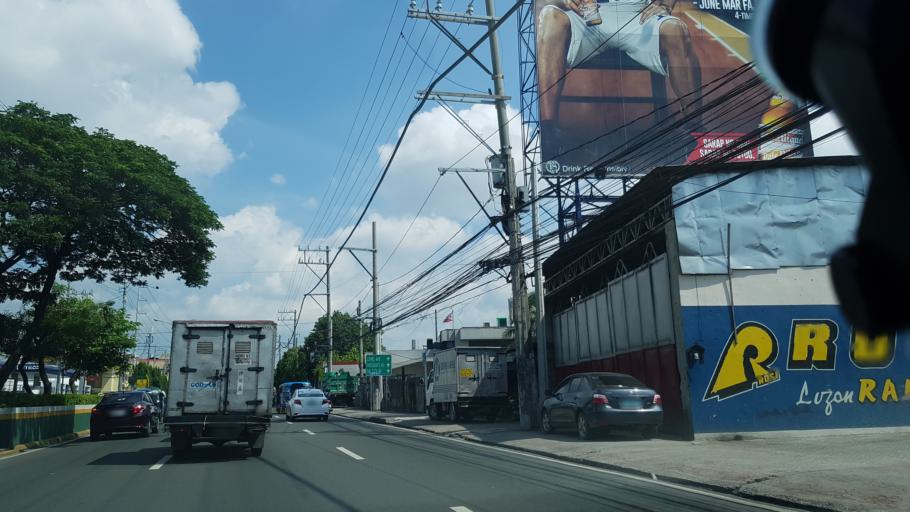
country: PH
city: Sambayanihan People's Village
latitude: 14.4724
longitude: 121.0055
